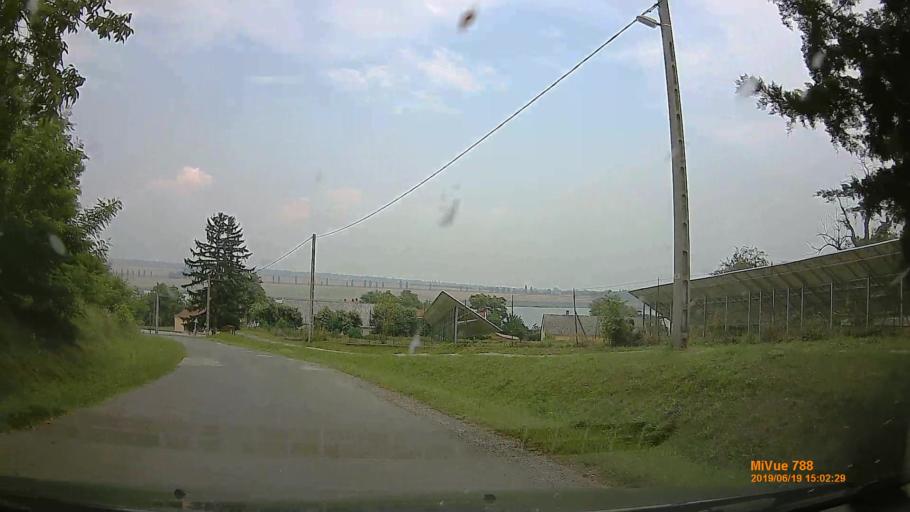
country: HU
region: Baranya
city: Szigetvar
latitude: 46.0899
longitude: 17.8025
